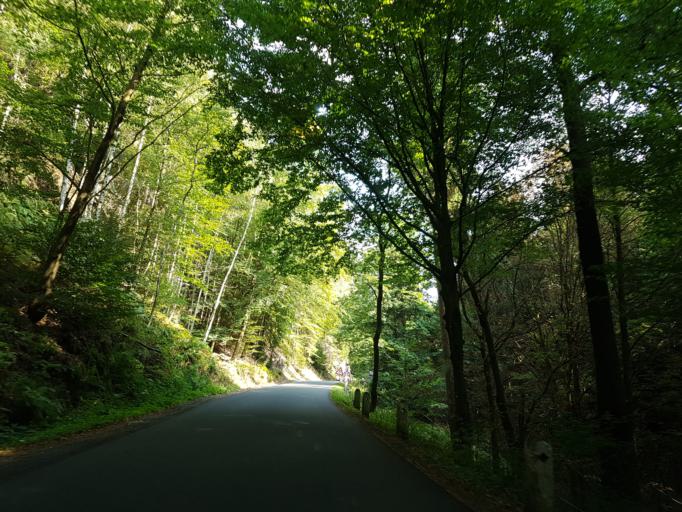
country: CZ
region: Ustecky
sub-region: Okres Decin
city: Decin
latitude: 50.8722
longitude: 14.2467
